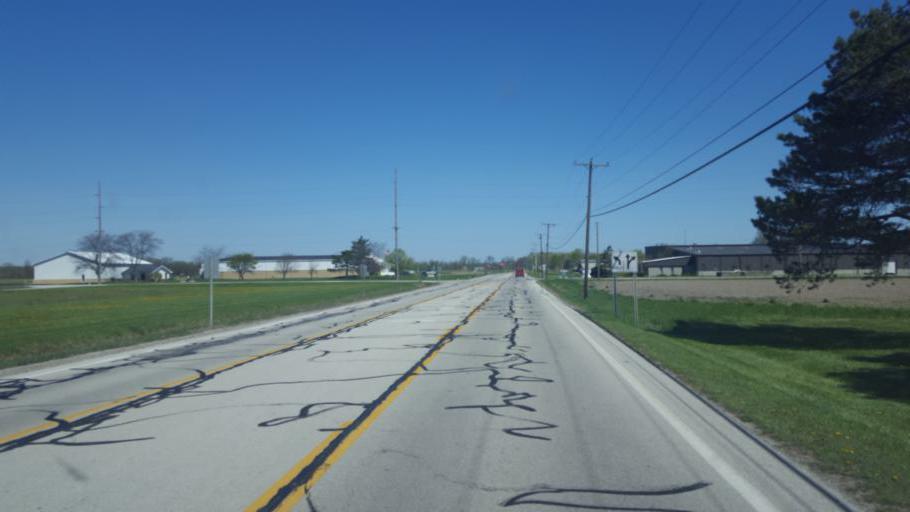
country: US
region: Ohio
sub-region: Ottawa County
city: Oak Harbor
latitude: 41.4420
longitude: -83.1353
